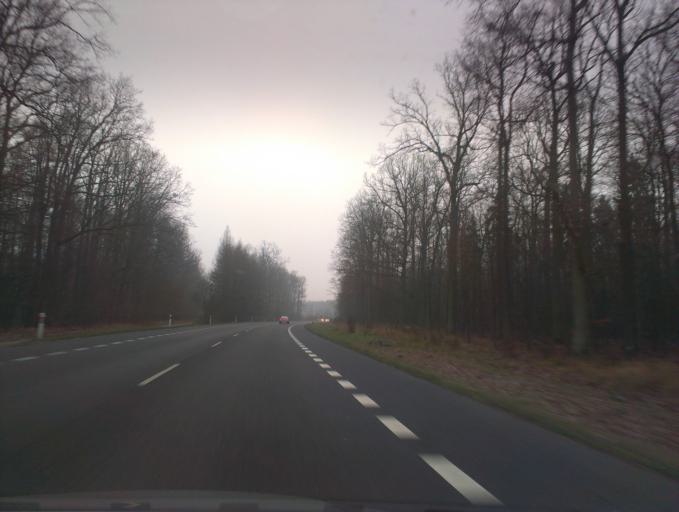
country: PL
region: Greater Poland Voivodeship
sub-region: Powiat chodzieski
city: Budzyn
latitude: 52.9129
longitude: 16.9731
